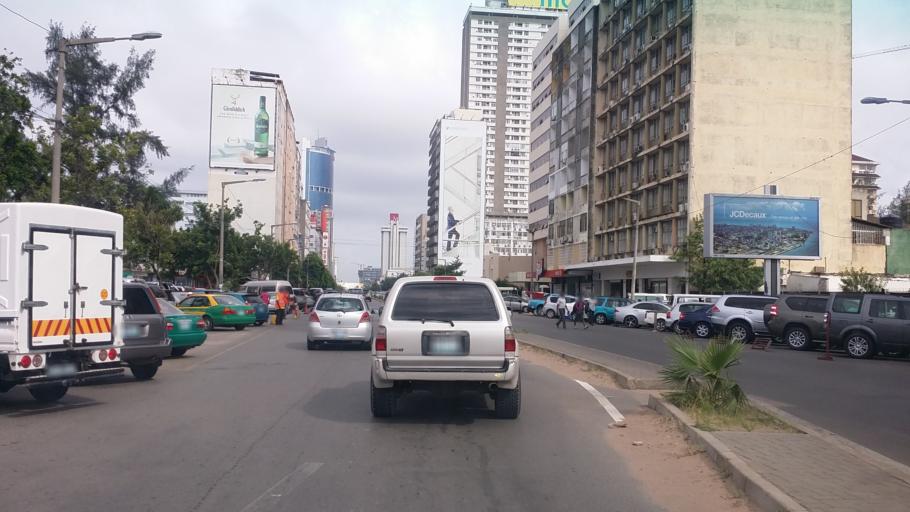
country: MZ
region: Maputo City
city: Maputo
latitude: -25.9759
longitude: 32.5763
